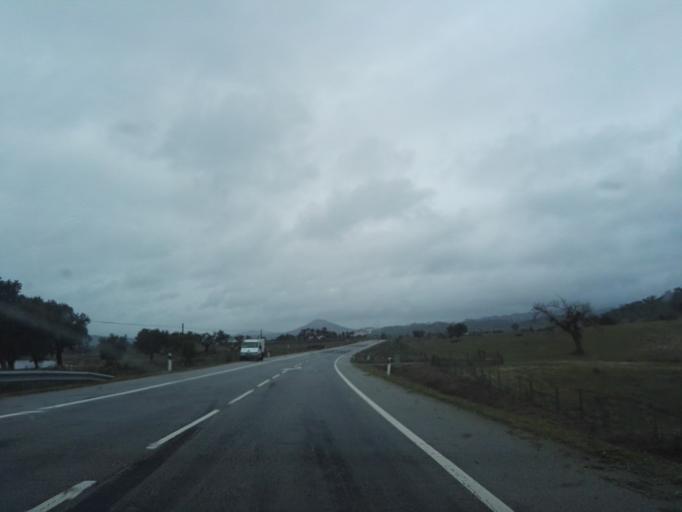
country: PT
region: Portalegre
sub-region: Portalegre
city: Urra
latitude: 39.2509
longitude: -7.4048
